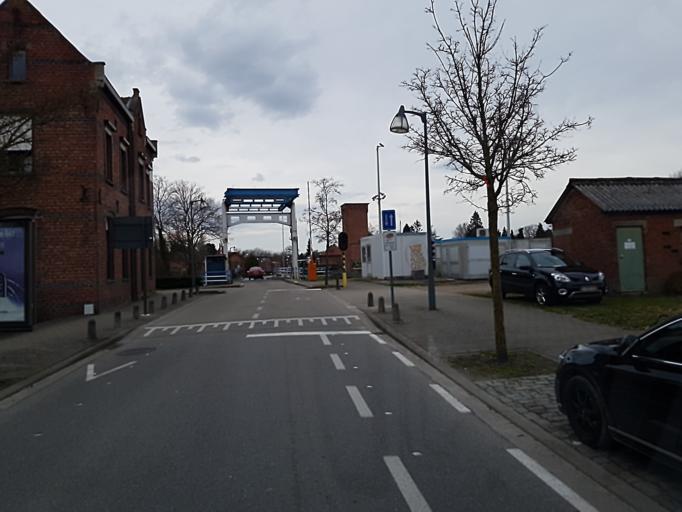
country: BE
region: Flanders
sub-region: Provincie Antwerpen
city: Turnhout
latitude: 51.3328
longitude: 4.9470
